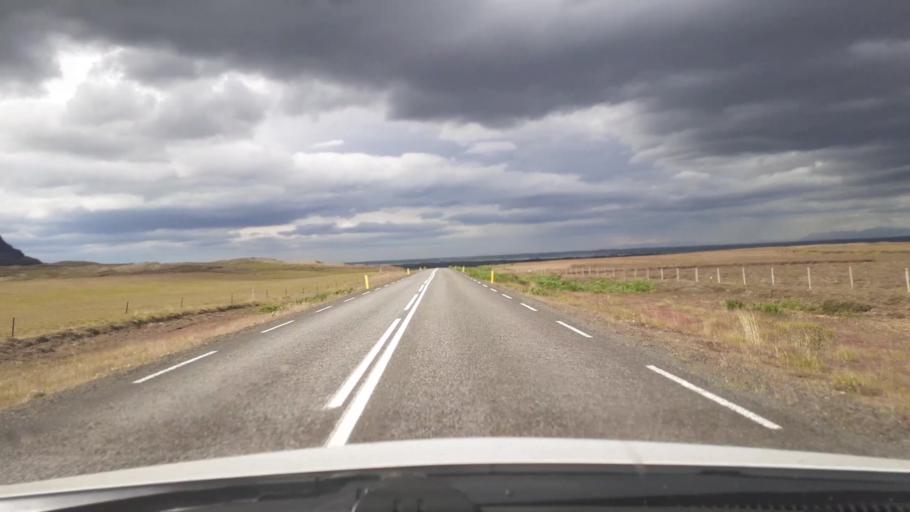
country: IS
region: West
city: Borgarnes
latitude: 64.5447
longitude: -21.6688
